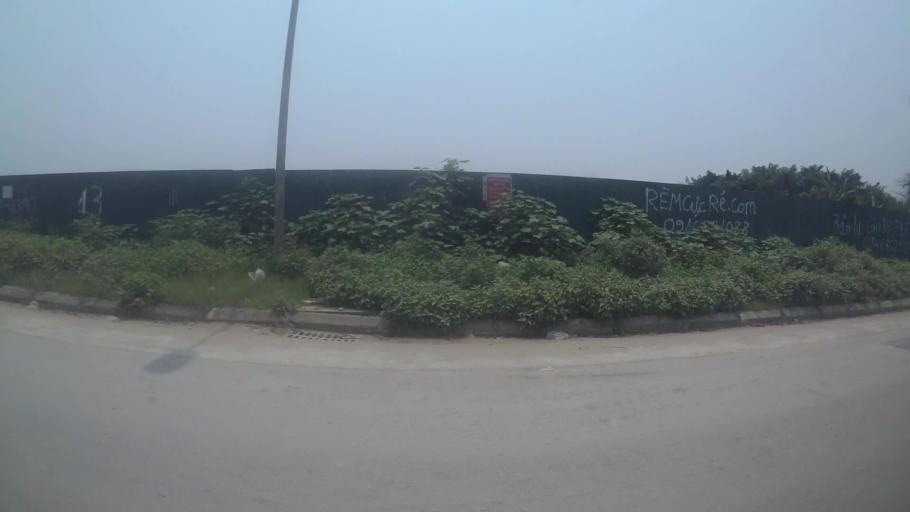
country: VN
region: Ha Noi
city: Thanh Xuan
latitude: 21.0038
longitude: 105.7720
